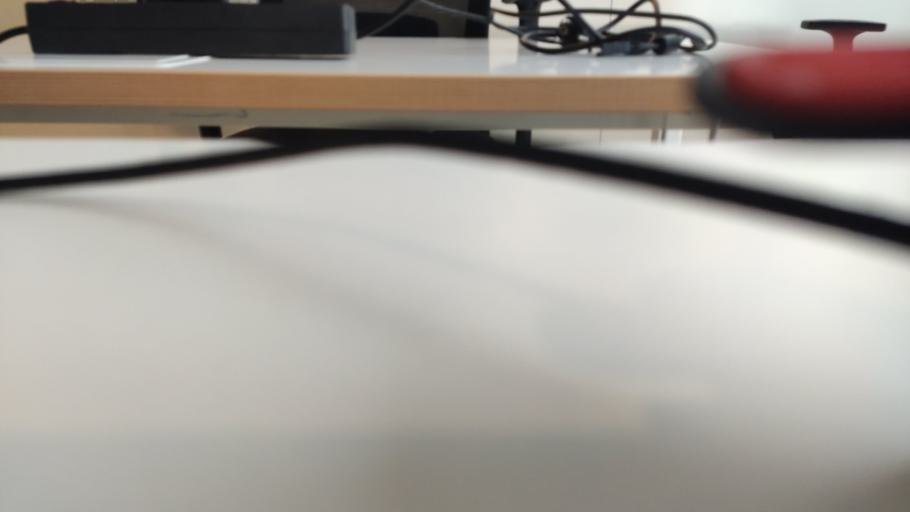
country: RU
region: Moskovskaya
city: Shevlyakovo
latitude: 56.4212
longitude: 36.9819
